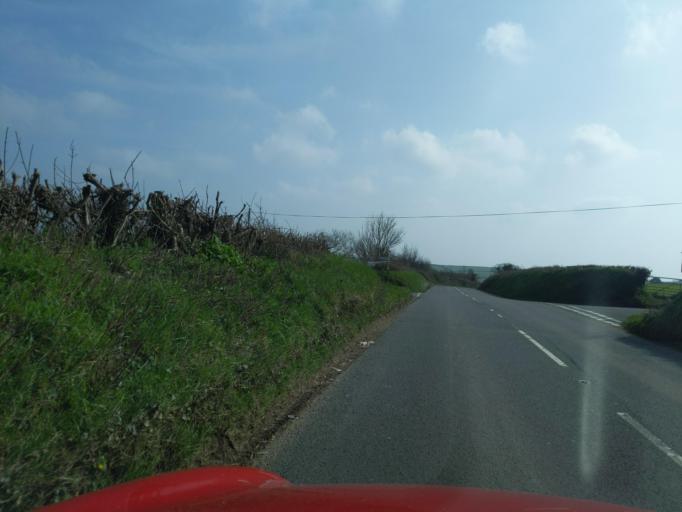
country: GB
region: England
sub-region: Devon
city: South Brent
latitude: 50.3967
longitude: -3.8456
